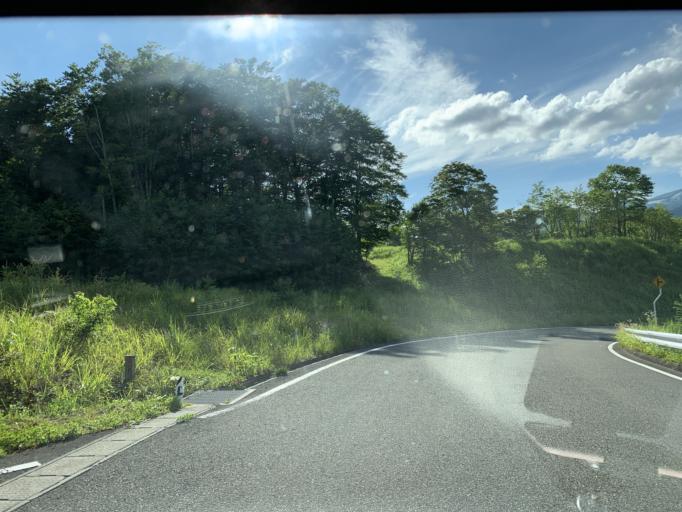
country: JP
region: Iwate
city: Ichinoseki
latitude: 38.9058
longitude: 140.8415
